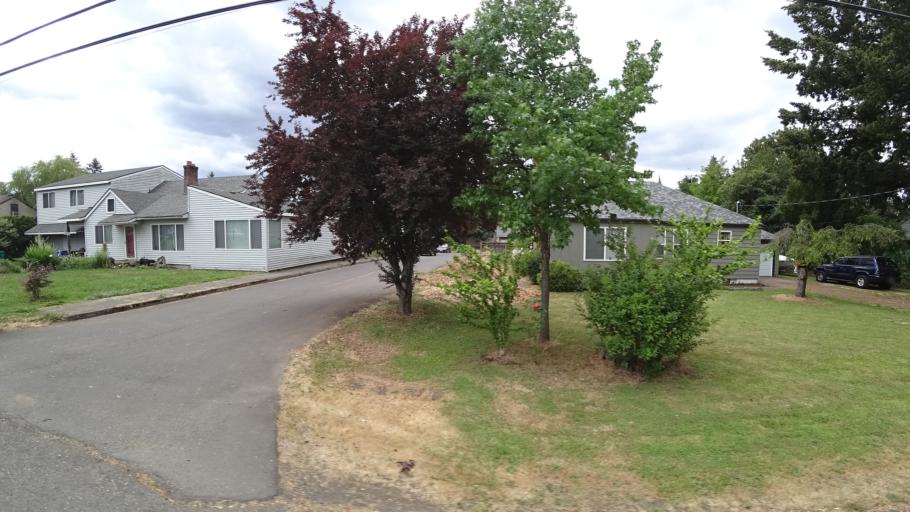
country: US
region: Oregon
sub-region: Clackamas County
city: Happy Valley
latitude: 45.4976
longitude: -122.5145
